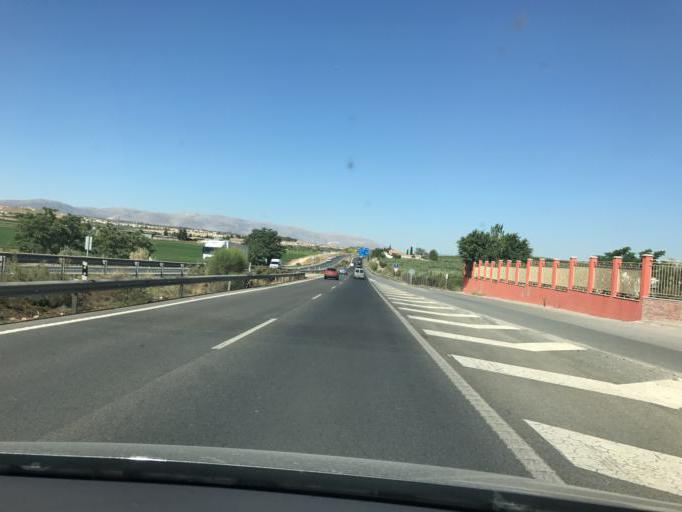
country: ES
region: Andalusia
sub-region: Provincia de Granada
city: Moraleda de Zafayona
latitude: 37.1807
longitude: -3.9355
